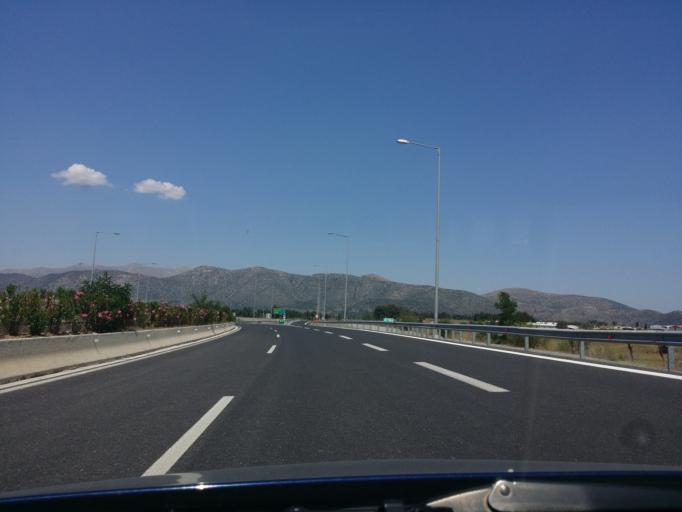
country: GR
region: Peloponnese
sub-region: Nomos Arkadias
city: Tripoli
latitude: 37.5014
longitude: 22.3973
